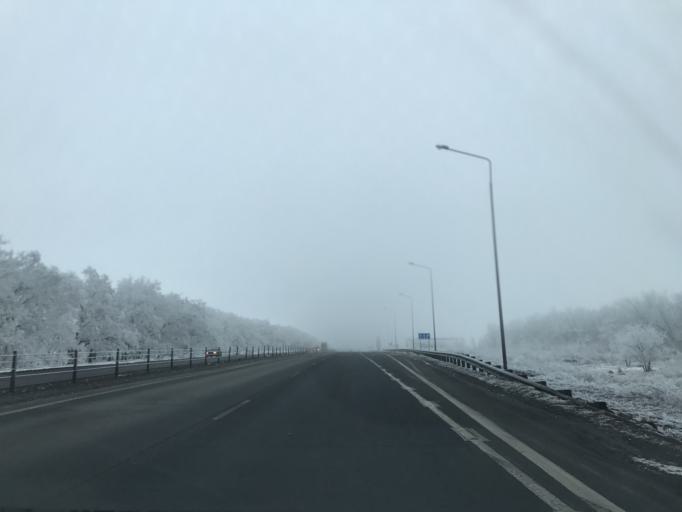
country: RU
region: Rostov
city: Likhoy
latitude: 48.1762
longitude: 40.2645
